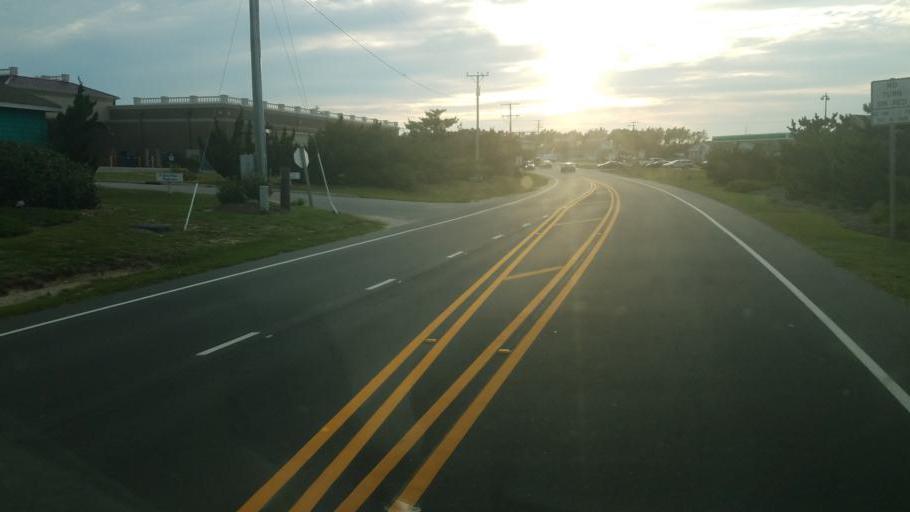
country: US
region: North Carolina
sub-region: Dare County
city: Kitty Hawk
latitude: 36.1001
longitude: -75.7123
